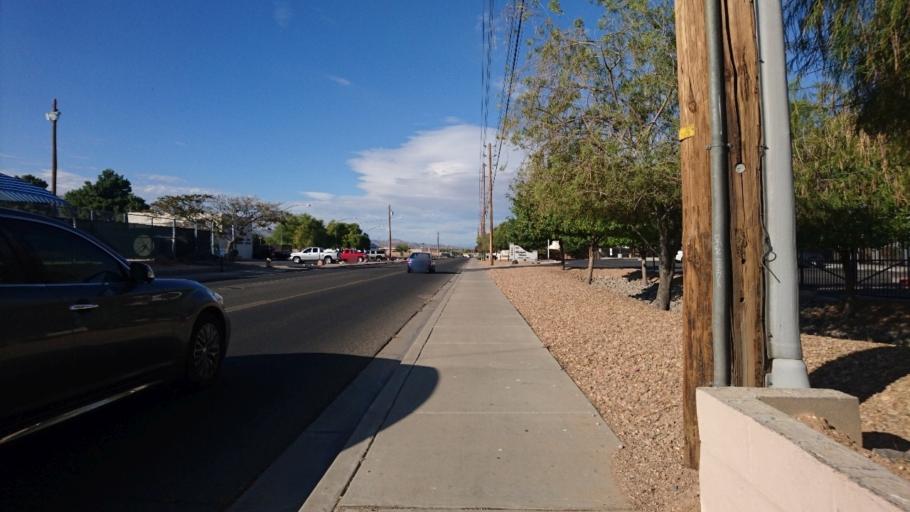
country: US
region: Arizona
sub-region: Mohave County
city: Kingman
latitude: 35.2203
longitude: -114.0247
